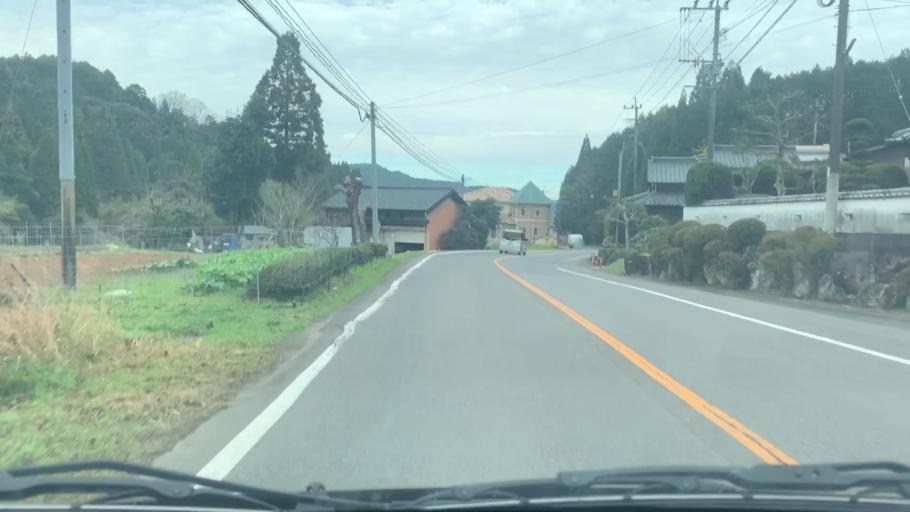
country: JP
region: Saga Prefecture
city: Takeocho-takeo
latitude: 33.1882
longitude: 129.9671
